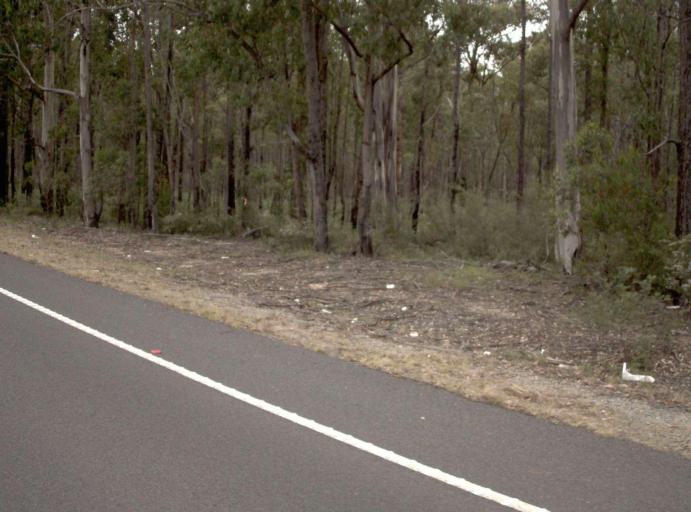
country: AU
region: Victoria
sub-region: East Gippsland
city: Lakes Entrance
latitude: -37.7297
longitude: 147.9326
